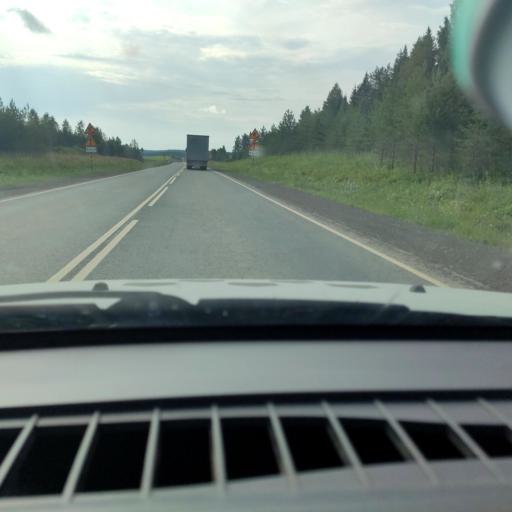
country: RU
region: Perm
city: Siva
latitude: 58.4240
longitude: 54.4545
